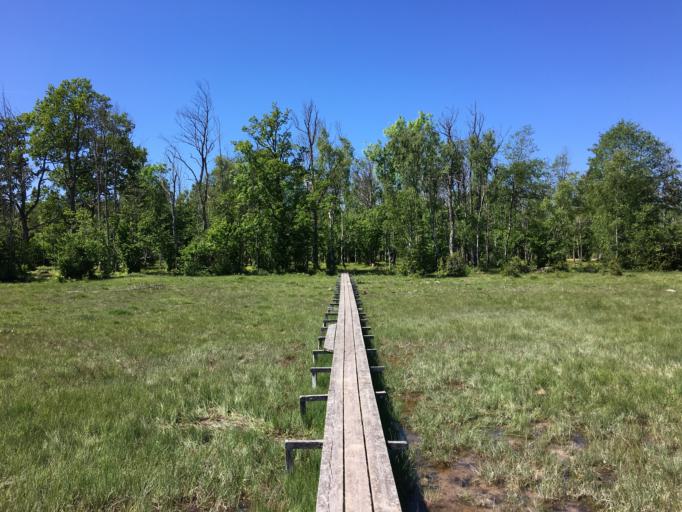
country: SE
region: Kalmar
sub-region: Borgholms Kommun
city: Borgholm
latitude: 56.7477
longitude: 16.6098
